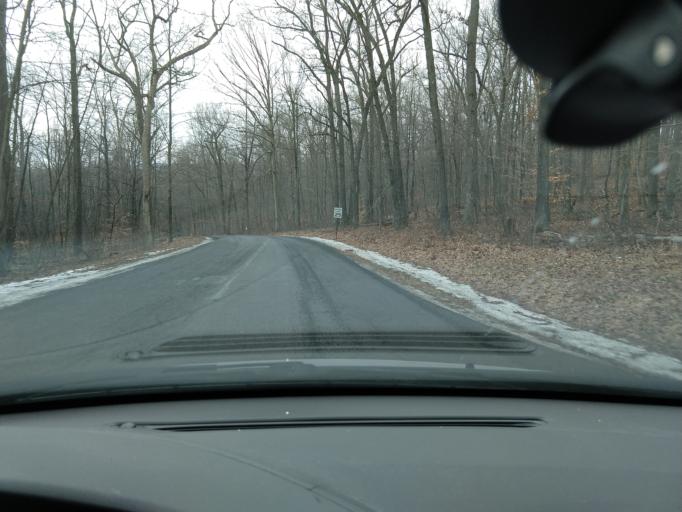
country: US
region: Pennsylvania
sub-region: Berks County
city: Birdsboro
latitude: 40.2081
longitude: -75.7885
